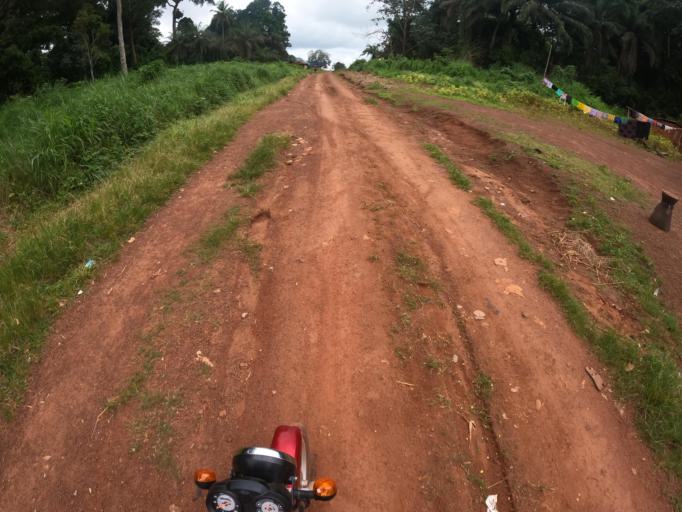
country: SL
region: Northern Province
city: Kamakwie
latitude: 9.5100
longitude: -12.2672
